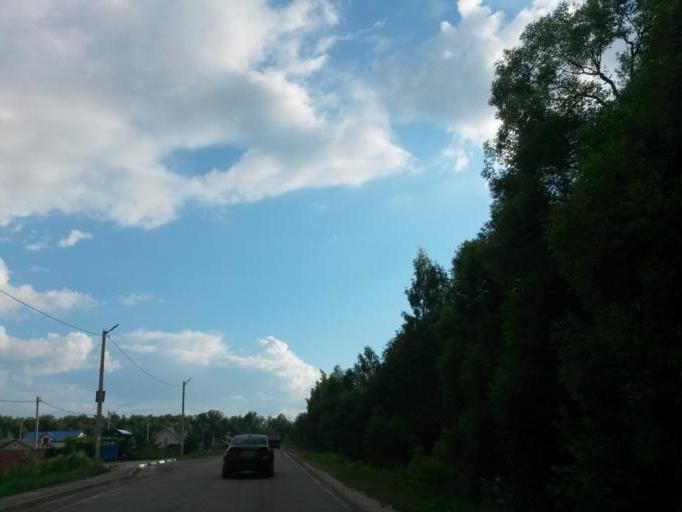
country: RU
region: Moskovskaya
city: Barybino
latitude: 55.2508
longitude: 37.8184
